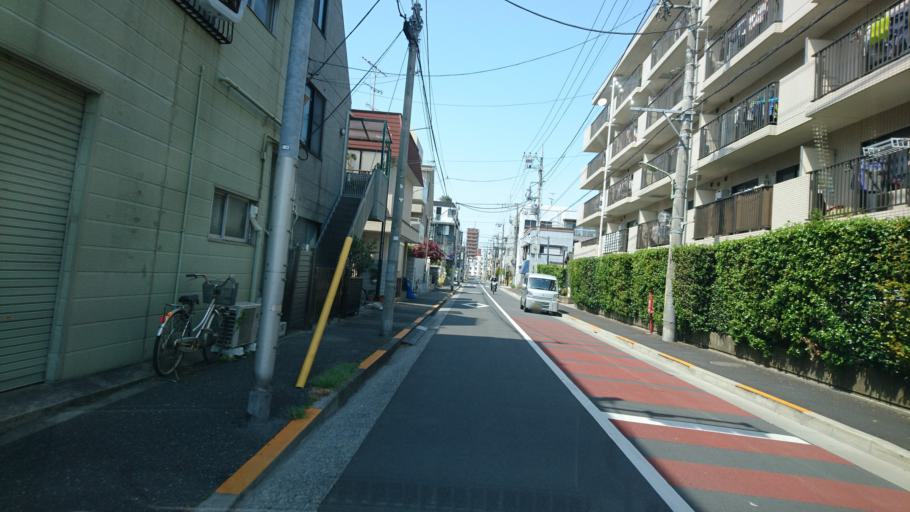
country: JP
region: Kanagawa
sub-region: Kawasaki-shi
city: Kawasaki
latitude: 35.5681
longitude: 139.7057
